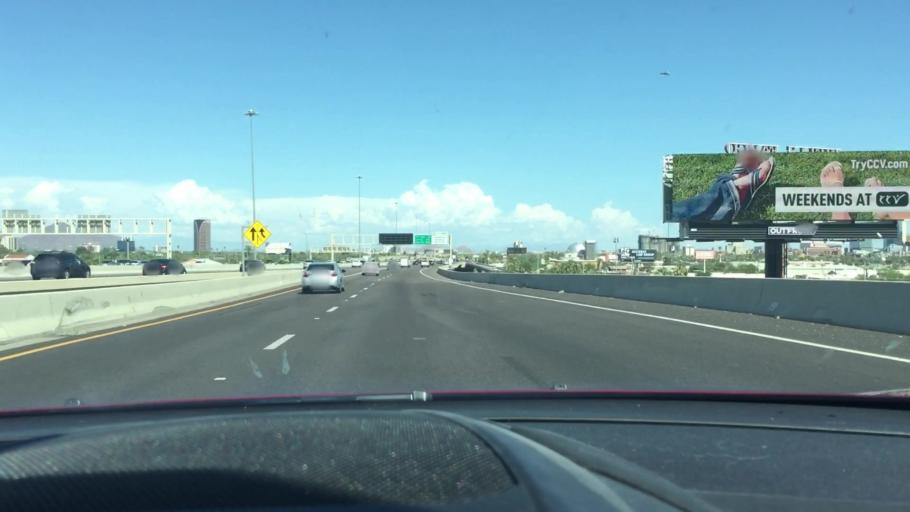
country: US
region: Arizona
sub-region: Maricopa County
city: Phoenix
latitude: 33.4611
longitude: -112.1026
